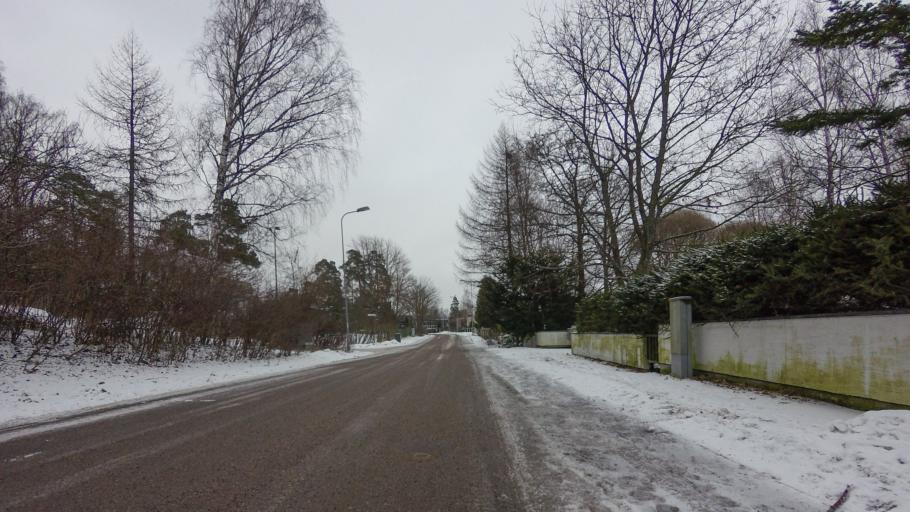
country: FI
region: Uusimaa
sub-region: Helsinki
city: Vantaa
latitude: 60.1990
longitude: 25.0777
